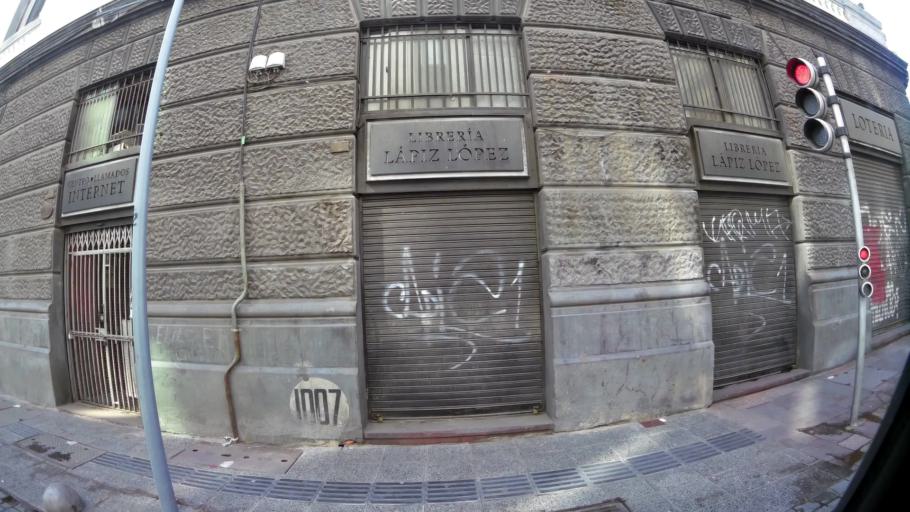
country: CL
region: Santiago Metropolitan
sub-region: Provincia de Santiago
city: Santiago
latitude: -33.4386
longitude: -70.6513
